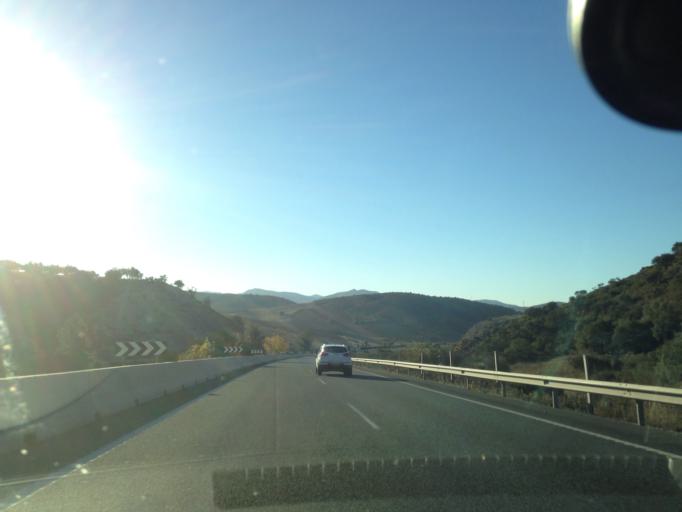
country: ES
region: Andalusia
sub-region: Provincia de Malaga
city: Casabermeja
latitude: 36.9466
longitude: -4.4416
